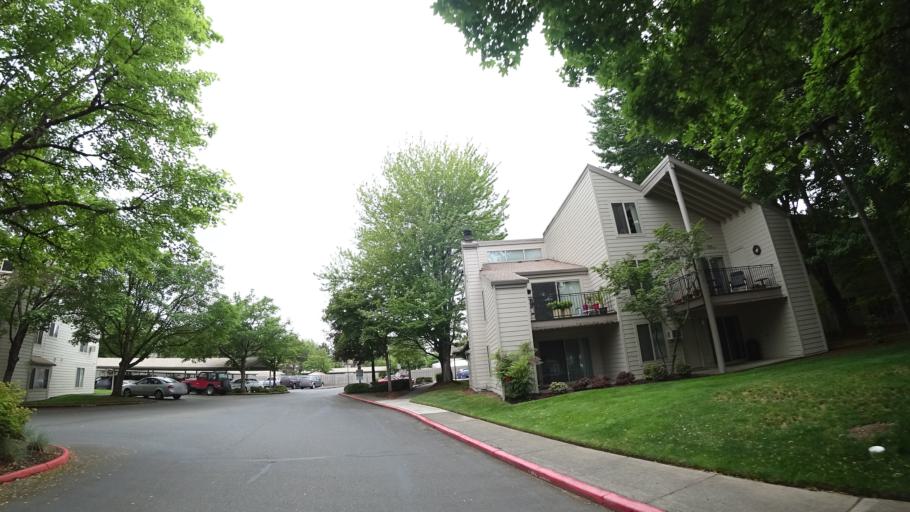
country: US
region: Oregon
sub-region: Washington County
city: Tigard
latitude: 45.4461
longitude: -122.7965
